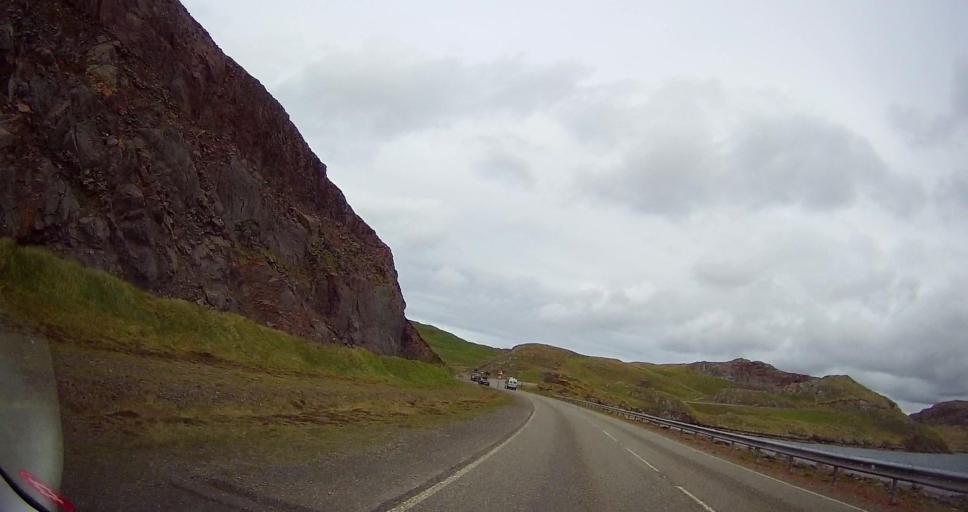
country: GB
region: Scotland
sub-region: Shetland Islands
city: Lerwick
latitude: 60.3963
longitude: -1.3809
